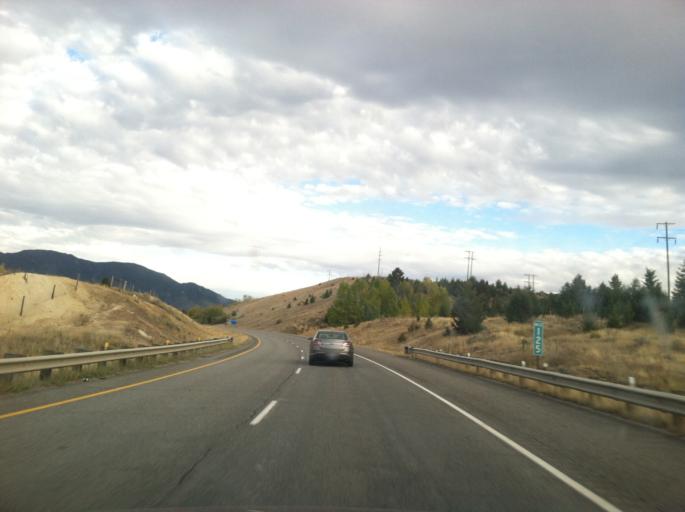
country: US
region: Montana
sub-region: Silver Bow County
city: Butte
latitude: 45.9962
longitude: -112.5657
